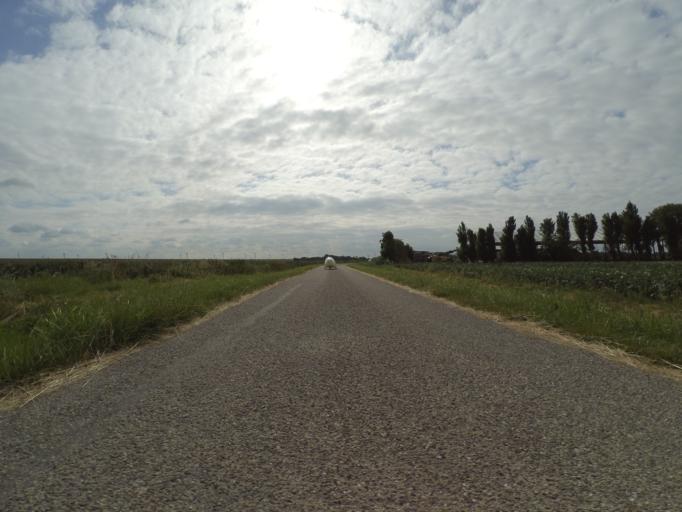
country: NL
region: Zeeland
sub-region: Gemeente Tholen
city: Tholen
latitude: 51.4355
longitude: 4.1836
